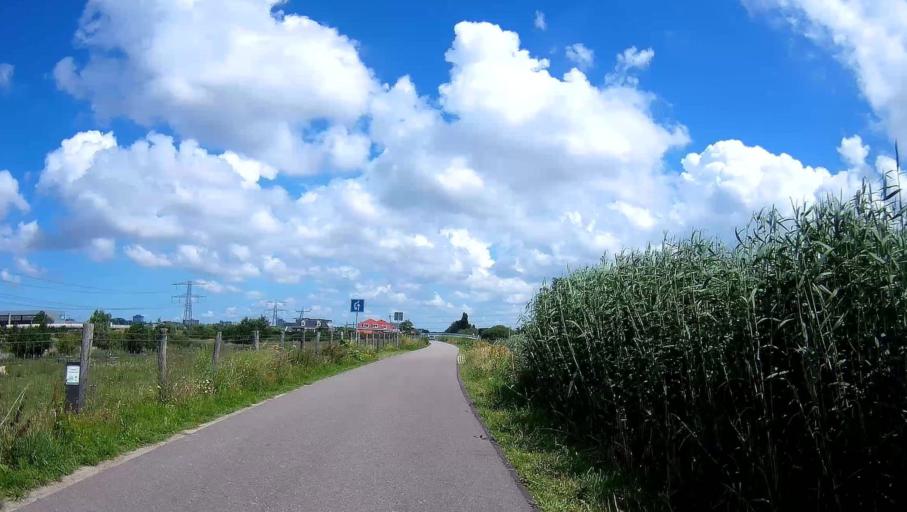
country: NL
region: South Holland
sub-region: Gemeente Westland
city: Kwintsheul
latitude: 52.0091
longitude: 4.2947
